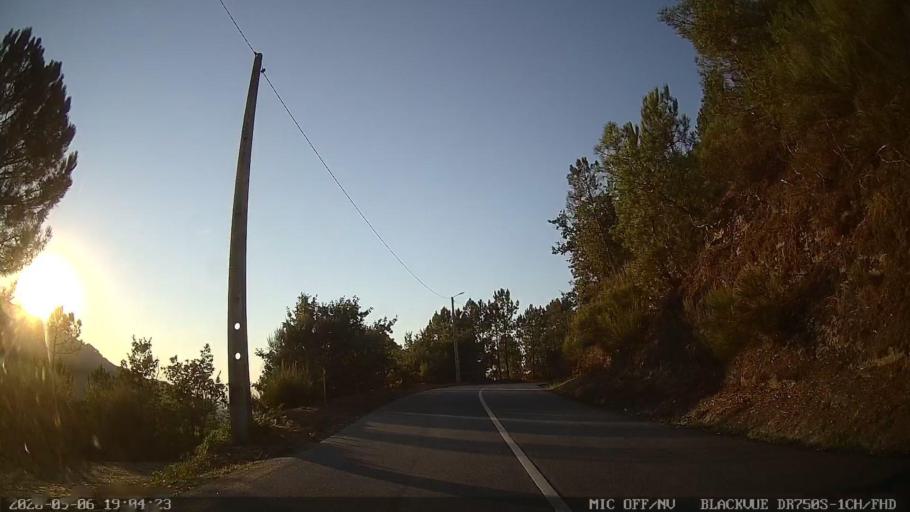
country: PT
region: Porto
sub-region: Baiao
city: Baiao
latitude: 41.2272
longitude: -7.9949
